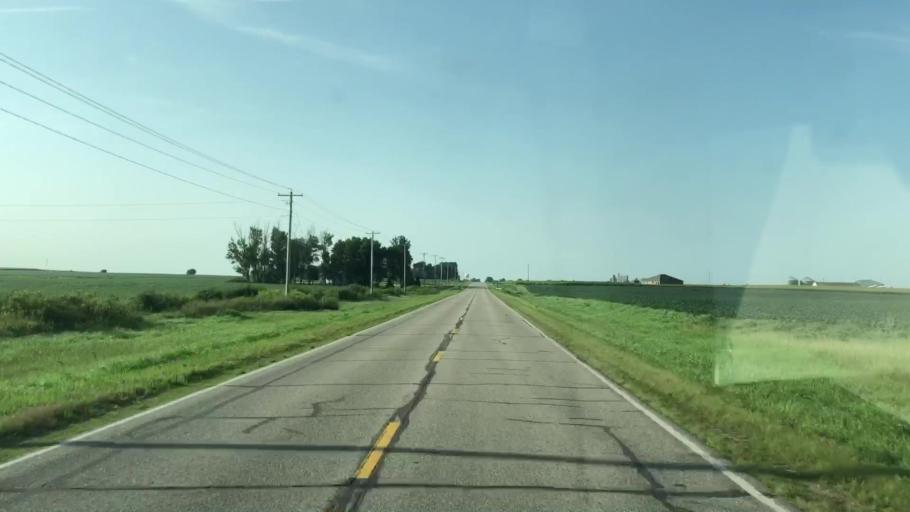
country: US
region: Iowa
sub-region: Lyon County
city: George
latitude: 43.3636
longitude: -95.9983
